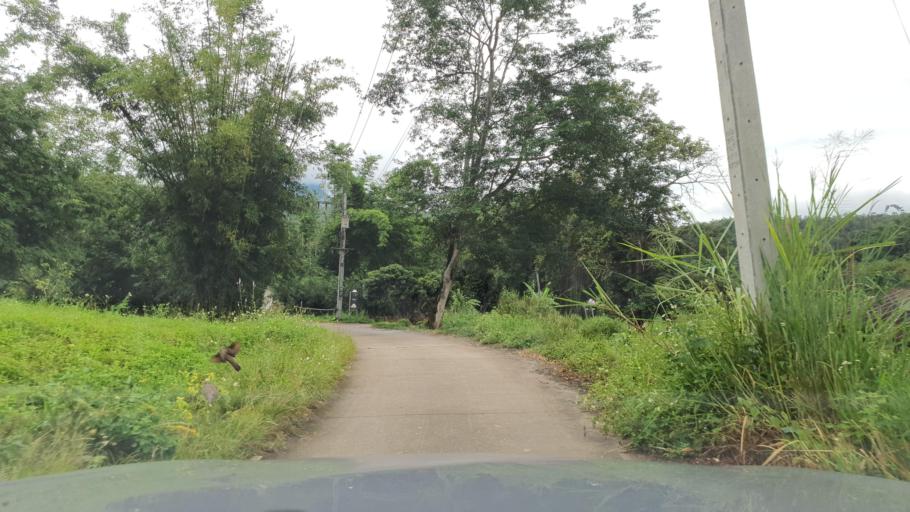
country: TH
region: Chiang Mai
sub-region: Amphoe Chiang Dao
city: Chiang Dao
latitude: 19.3321
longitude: 98.9288
